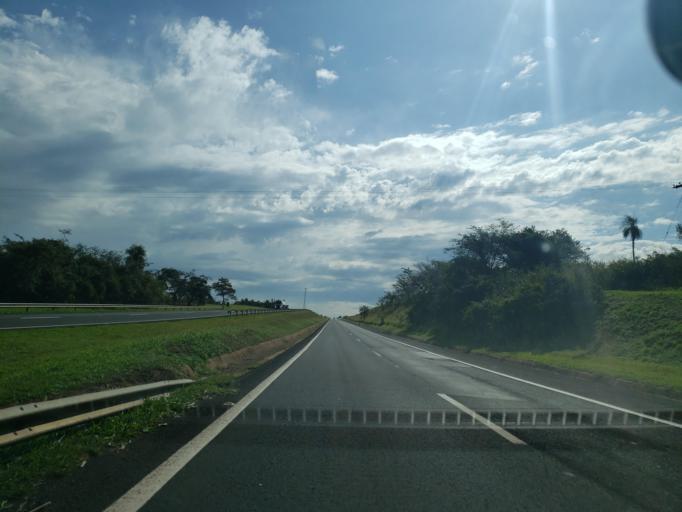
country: BR
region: Sao Paulo
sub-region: Cafelandia
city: Cafelandia
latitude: -21.8893
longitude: -49.5431
